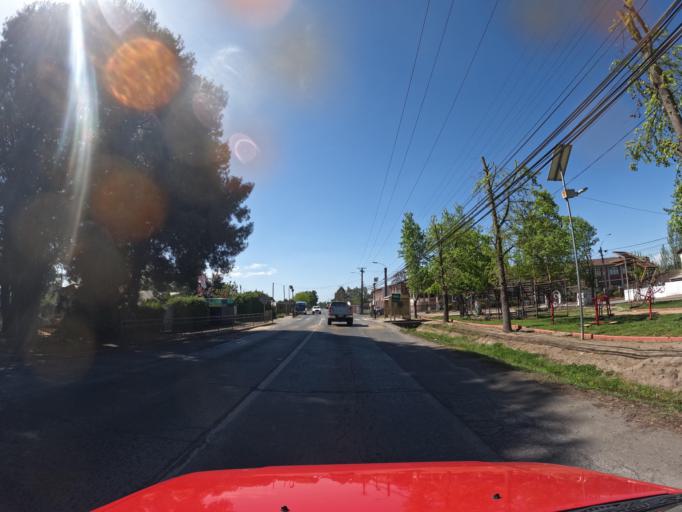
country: CL
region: Maule
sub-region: Provincia de Curico
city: Molina
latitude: -35.0729
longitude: -71.2565
